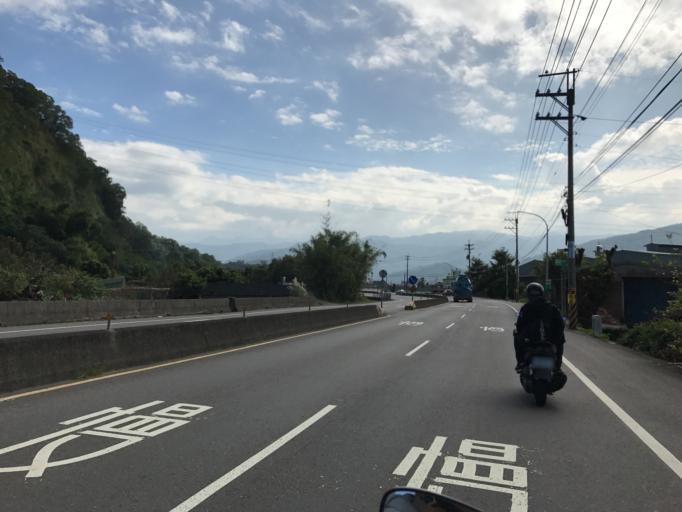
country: TW
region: Taiwan
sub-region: Hsinchu
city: Zhubei
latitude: 24.7326
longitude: 121.1220
